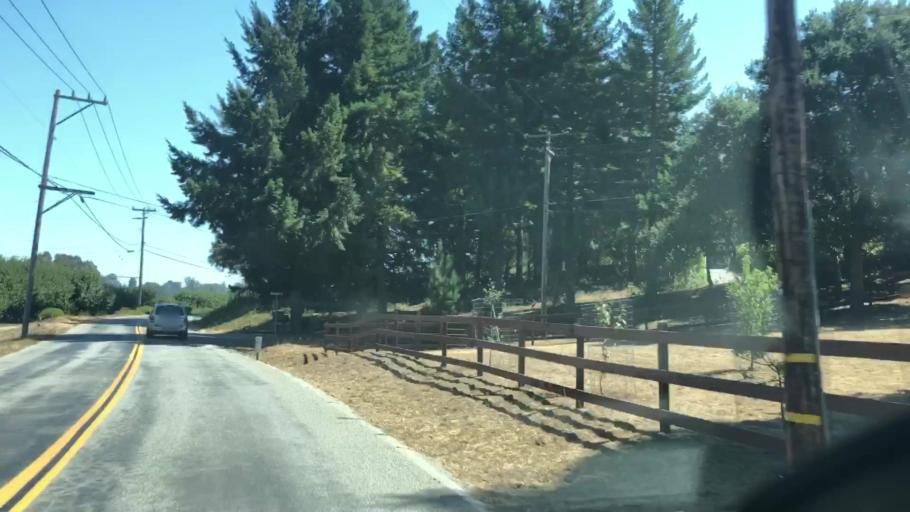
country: US
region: California
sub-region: Santa Cruz County
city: Corralitos
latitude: 36.9970
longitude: -121.8056
